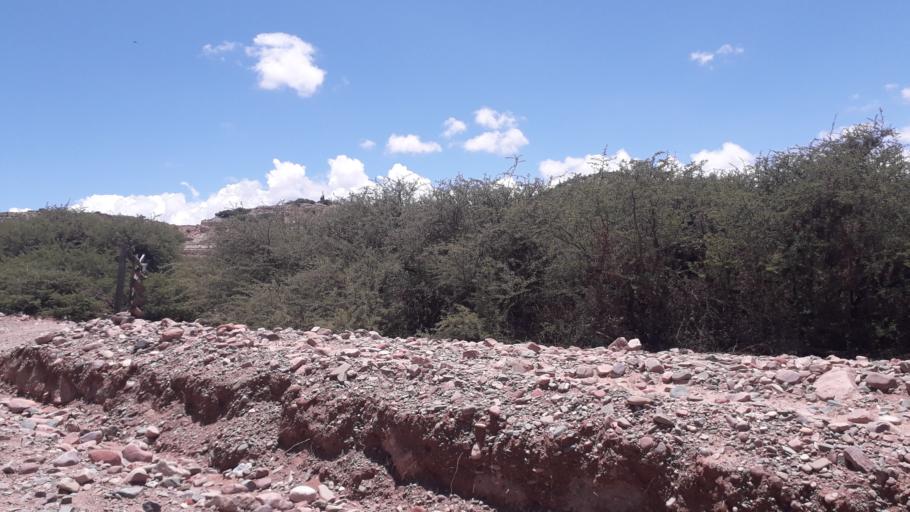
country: AR
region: Jujuy
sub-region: Departamento de Humahuaca
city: Humahuaca
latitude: -23.1940
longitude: -65.3440
